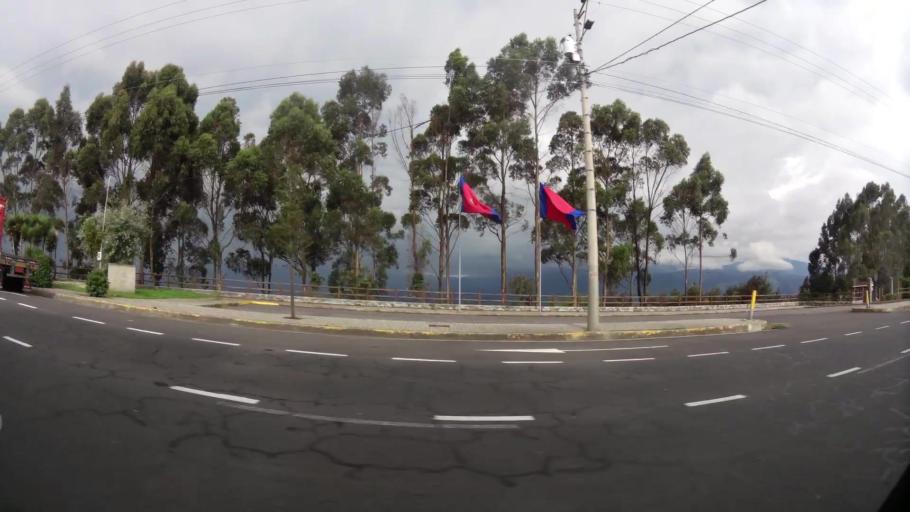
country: EC
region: Pichincha
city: Sangolqui
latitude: -0.3409
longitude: -78.5216
